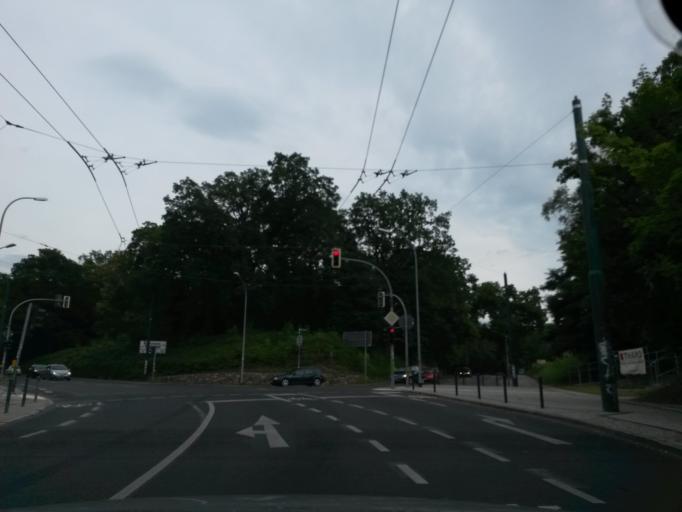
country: DE
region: Brandenburg
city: Eberswalde
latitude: 52.8296
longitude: 13.8279
